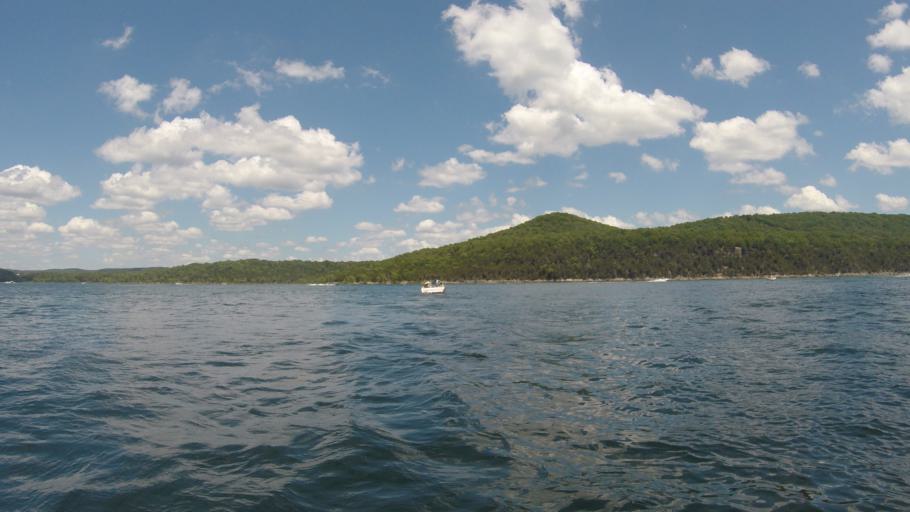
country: US
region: Missouri
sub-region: Barry County
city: Shell Knob
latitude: 36.5961
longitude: -93.5455
